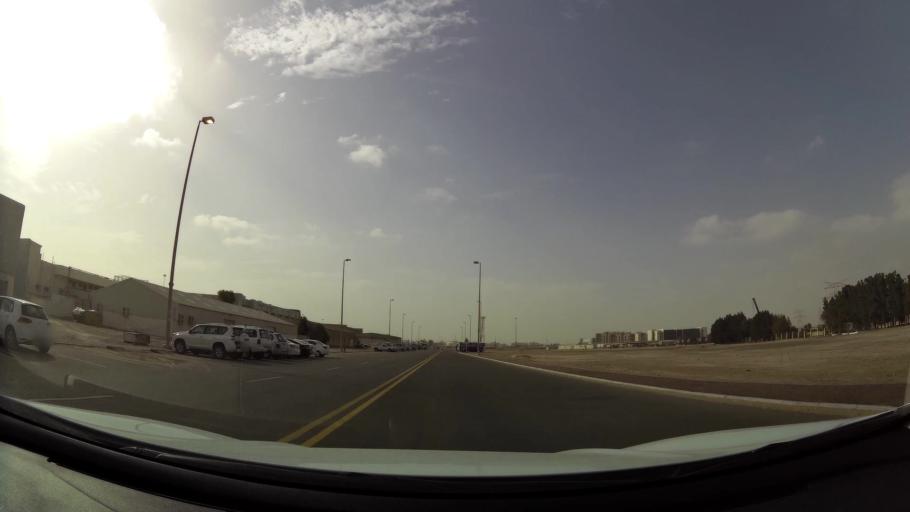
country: AE
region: Abu Dhabi
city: Abu Dhabi
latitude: 24.4097
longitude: 54.5187
